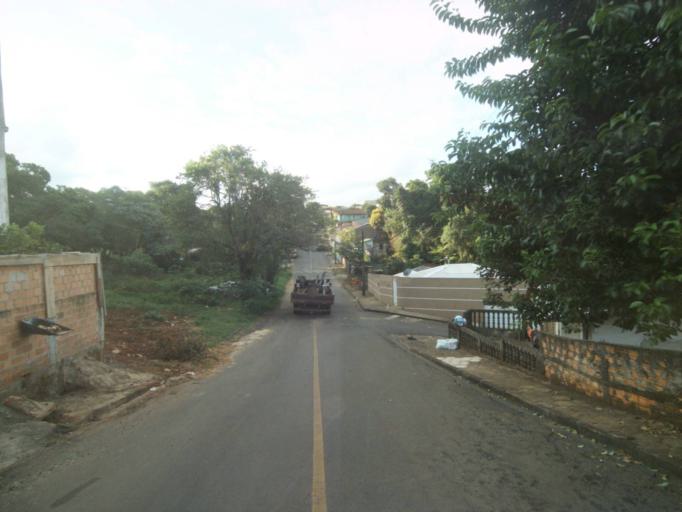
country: BR
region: Parana
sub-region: Telemaco Borba
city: Telemaco Borba
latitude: -24.3263
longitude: -50.6385
